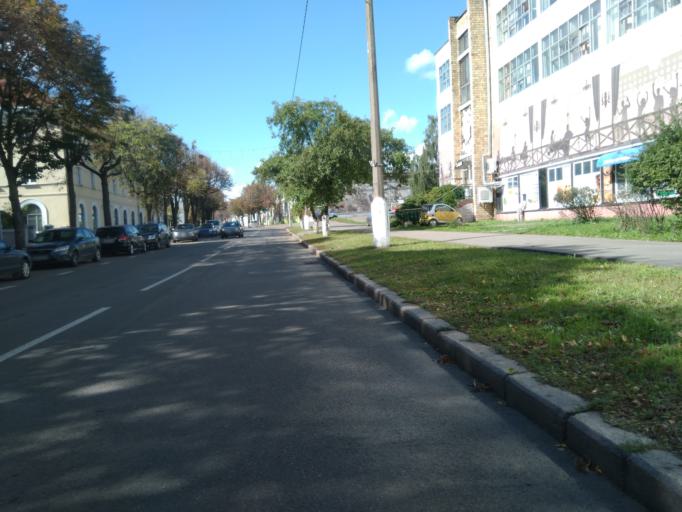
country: BY
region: Minsk
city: Minsk
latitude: 53.8951
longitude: 27.5758
